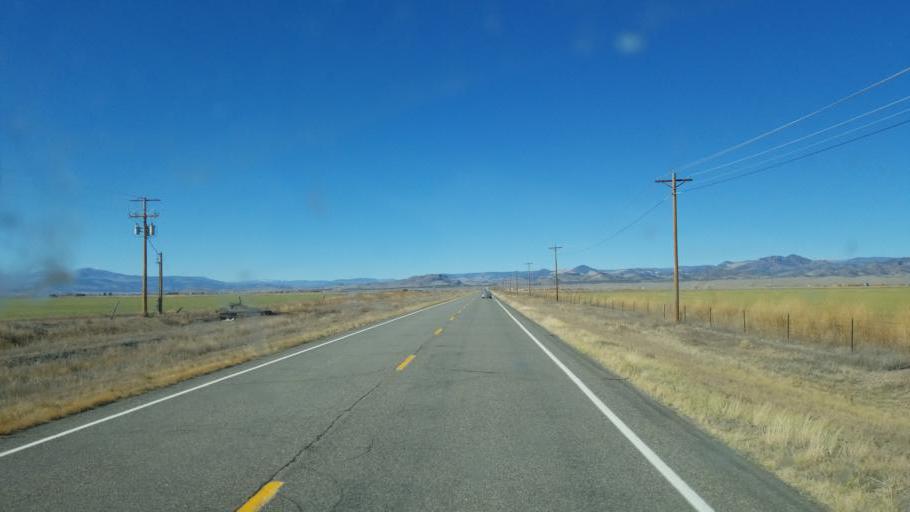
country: US
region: Colorado
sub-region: Saguache County
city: Center
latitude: 37.7482
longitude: -106.2066
